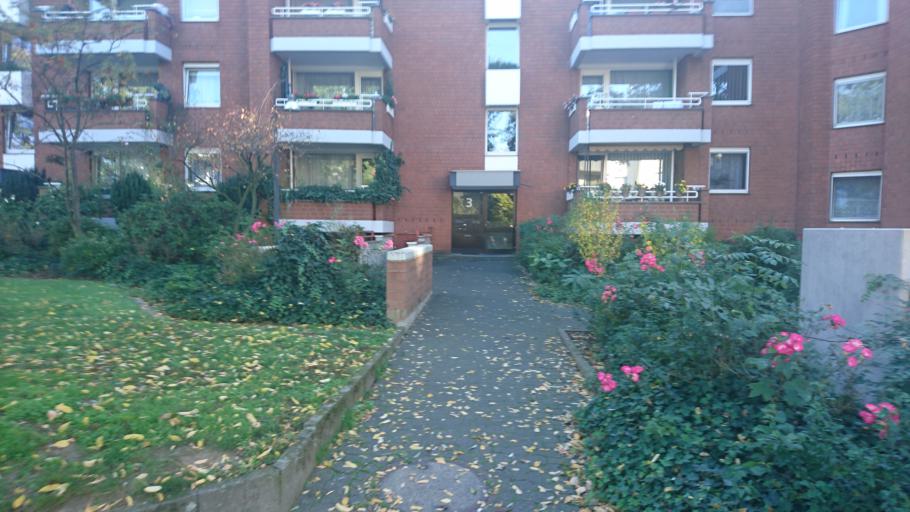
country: DE
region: North Rhine-Westphalia
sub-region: Regierungsbezirk Dusseldorf
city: Hilden
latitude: 51.1615
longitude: 6.8888
